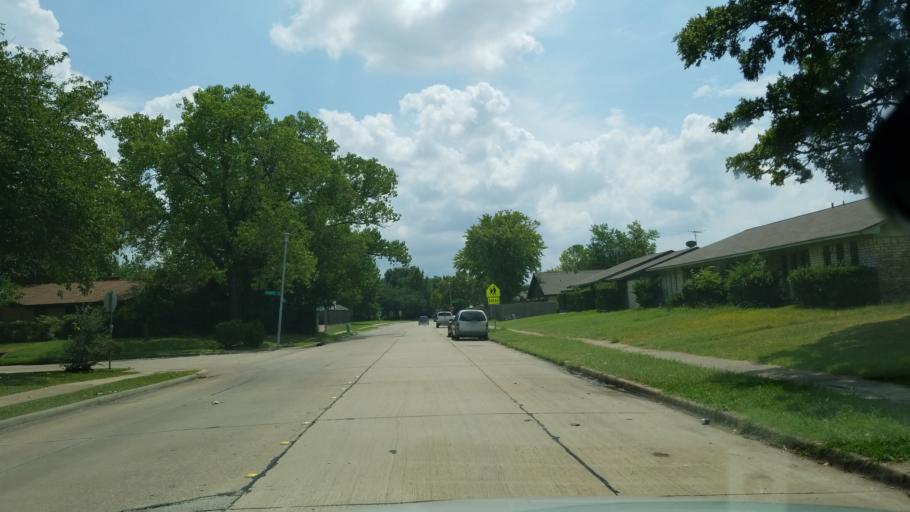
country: US
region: Texas
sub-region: Dallas County
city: Garland
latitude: 32.9254
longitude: -96.6574
